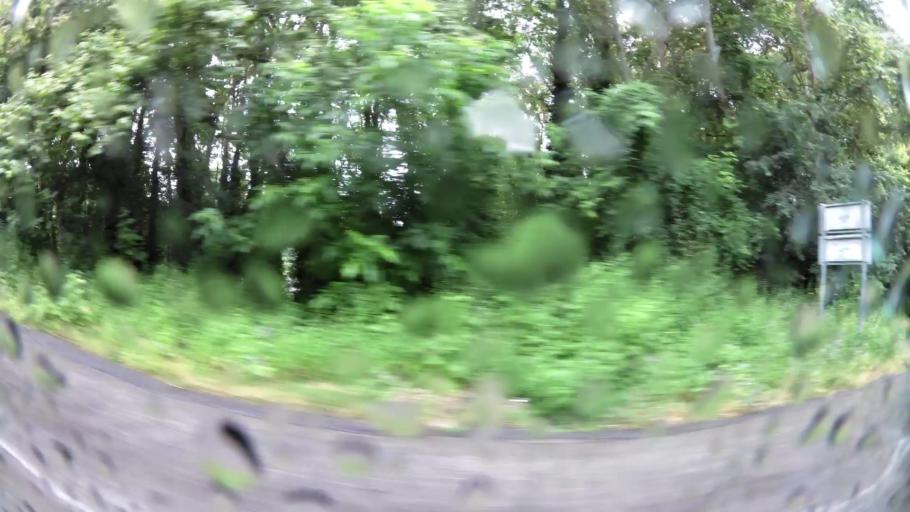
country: GR
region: Central Macedonia
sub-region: Nomos Imathias
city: Veroia
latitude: 40.5307
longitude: 22.1973
